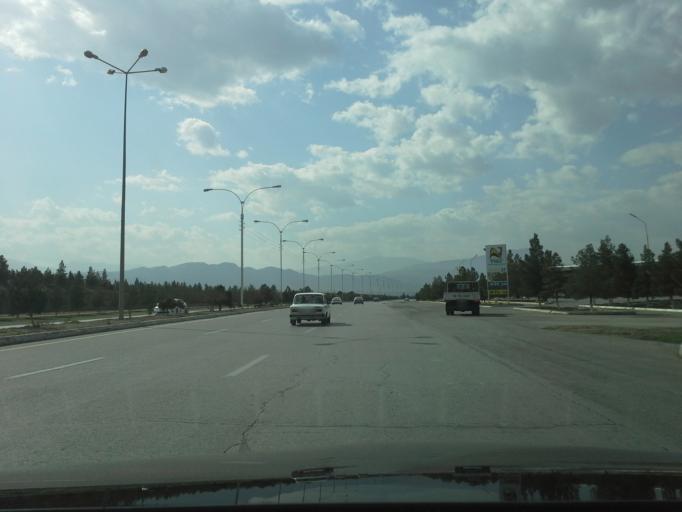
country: TM
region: Ahal
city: Ashgabat
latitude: 37.9708
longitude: 58.2753
